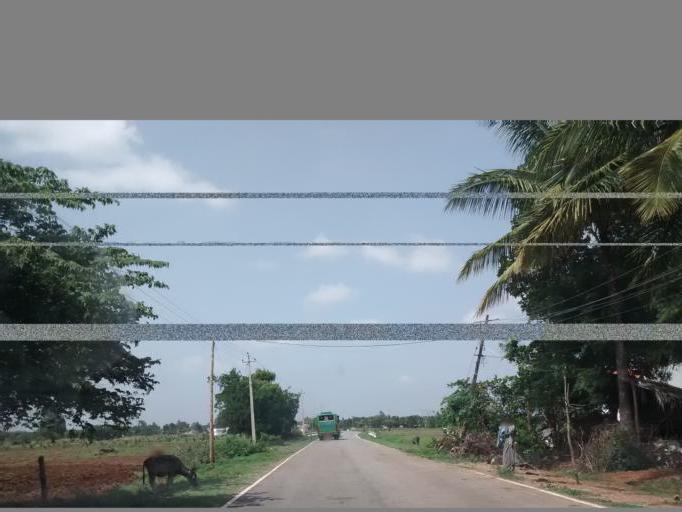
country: IN
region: Karnataka
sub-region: Hassan
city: Hole Narsipur
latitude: 12.6651
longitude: 76.1836
